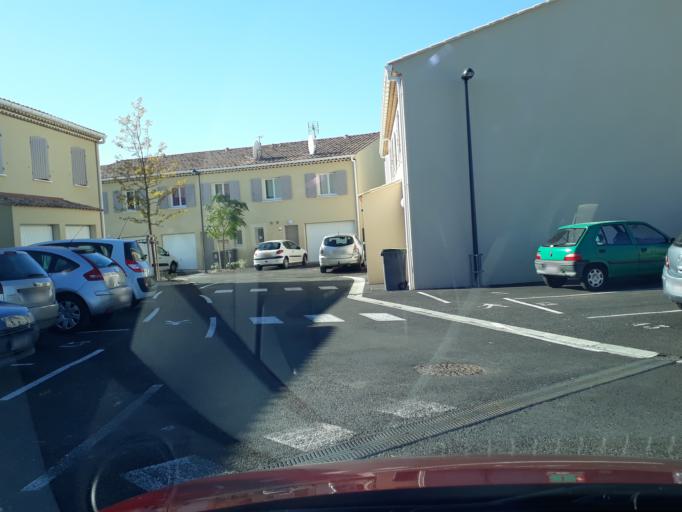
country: FR
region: Provence-Alpes-Cote d'Azur
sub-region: Departement du Vaucluse
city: Carpentras
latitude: 44.0588
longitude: 5.0709
